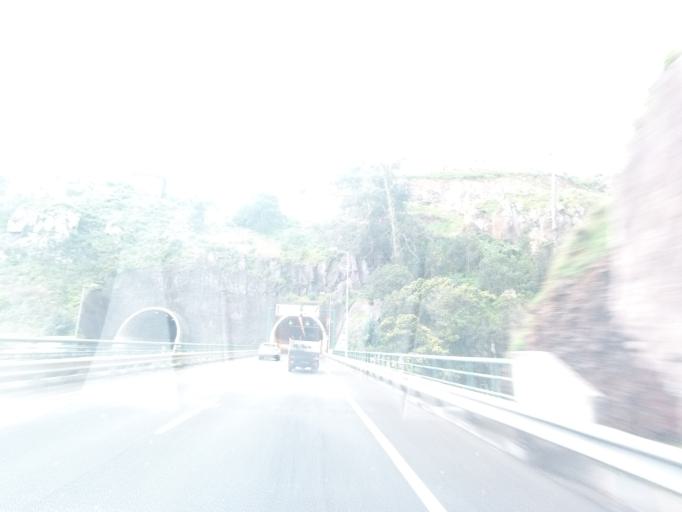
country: PT
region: Madeira
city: Canico
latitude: 32.6485
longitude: -16.8506
